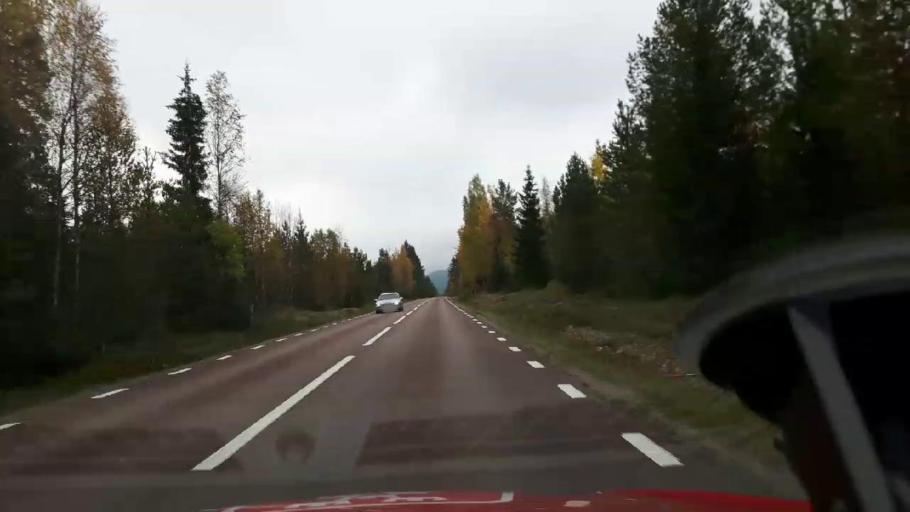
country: SE
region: Jaemtland
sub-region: Harjedalens Kommun
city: Sveg
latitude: 62.3277
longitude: 14.7394
